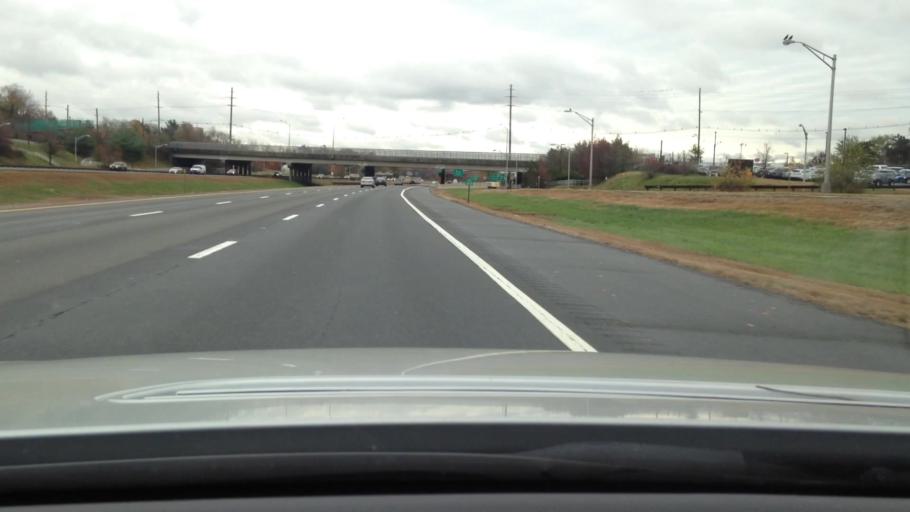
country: US
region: New Jersey
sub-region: Bergen County
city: Paramus
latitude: 40.9661
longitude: -74.0654
